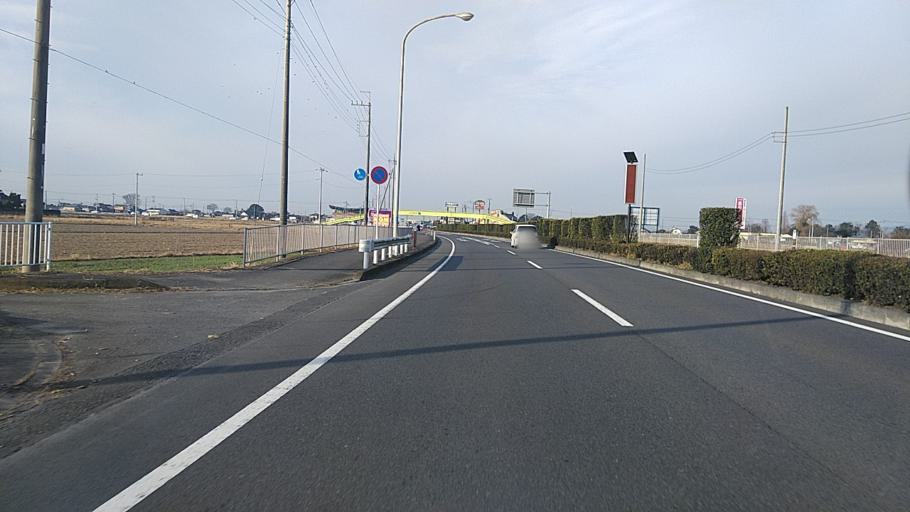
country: JP
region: Tochigi
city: Oyama
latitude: 36.3104
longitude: 139.7768
